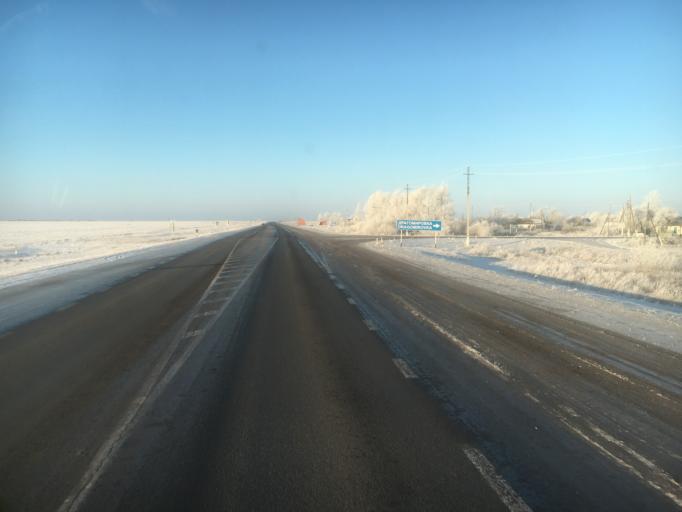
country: KZ
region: Soltustik Qazaqstan
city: Taiynsha
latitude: 53.7494
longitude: 69.3630
